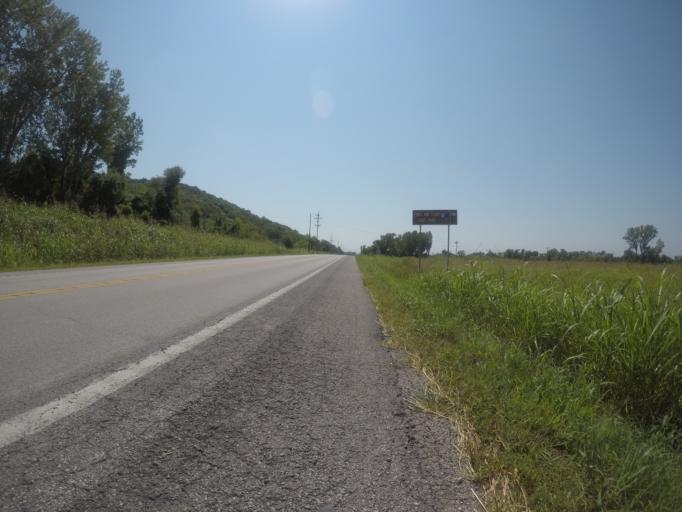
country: US
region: Kansas
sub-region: Atchison County
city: Atchison
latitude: 39.5431
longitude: -95.0431
